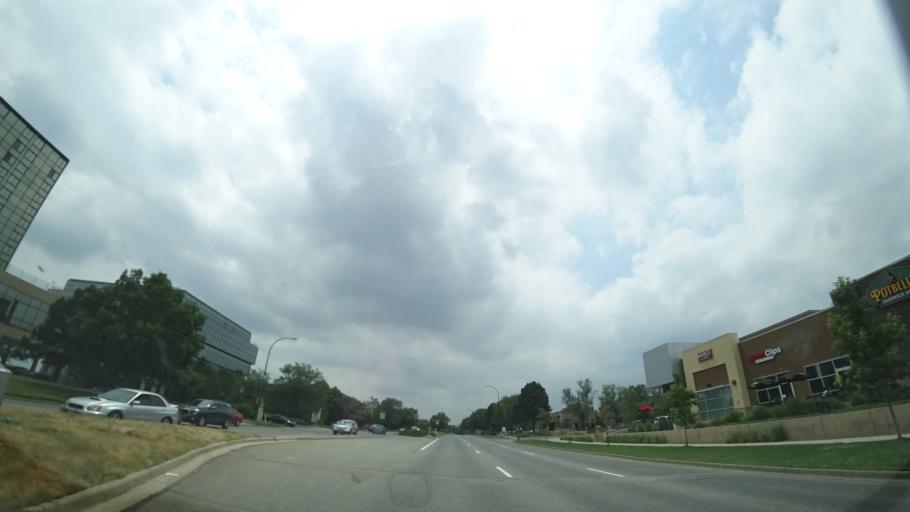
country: US
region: Colorado
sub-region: Jefferson County
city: Applewood
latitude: 39.7219
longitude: -105.1325
